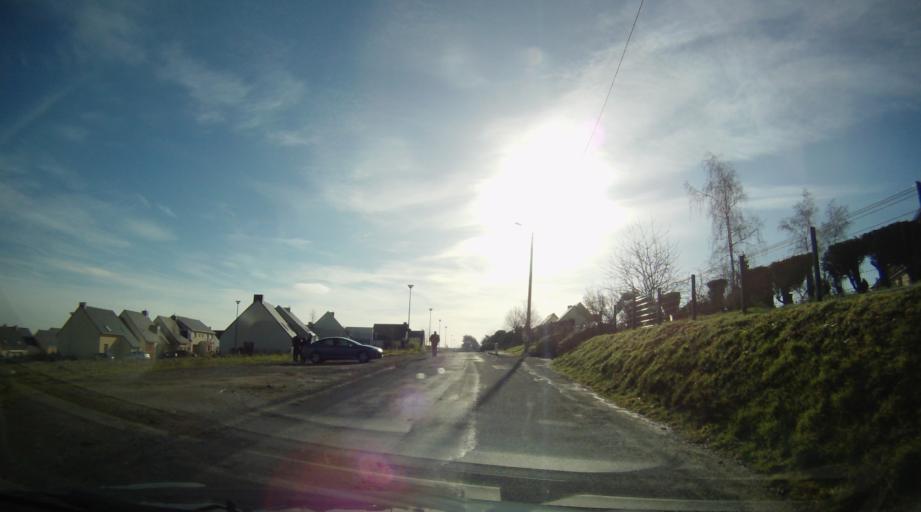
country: FR
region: Brittany
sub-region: Departement d'Ille-et-Vilaine
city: Bourgbarre
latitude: 47.9917
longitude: -1.6103
